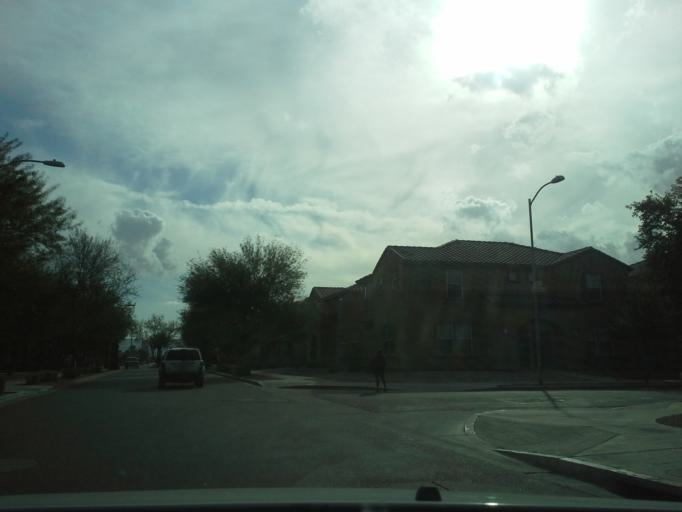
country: US
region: Arizona
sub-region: Maricopa County
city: Phoenix
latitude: 33.4384
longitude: -112.0847
